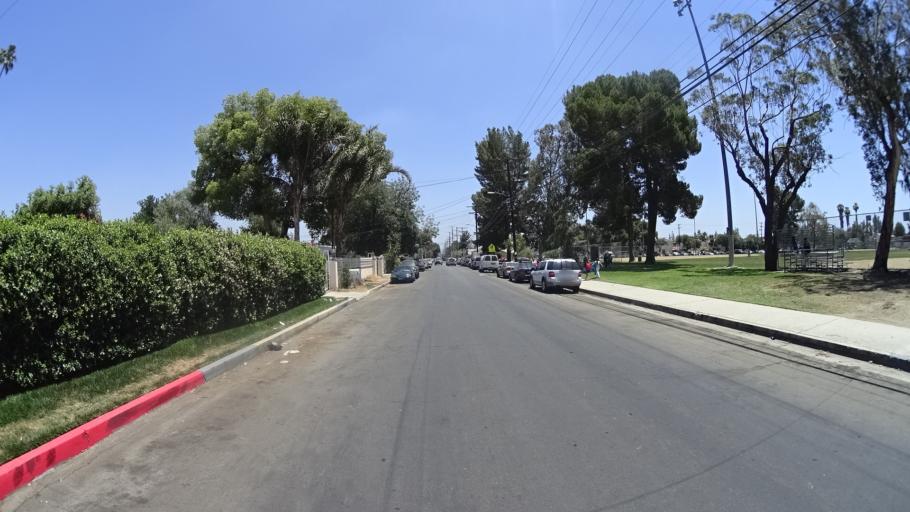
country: US
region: California
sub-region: Los Angeles County
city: Van Nuys
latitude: 34.2319
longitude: -118.4591
